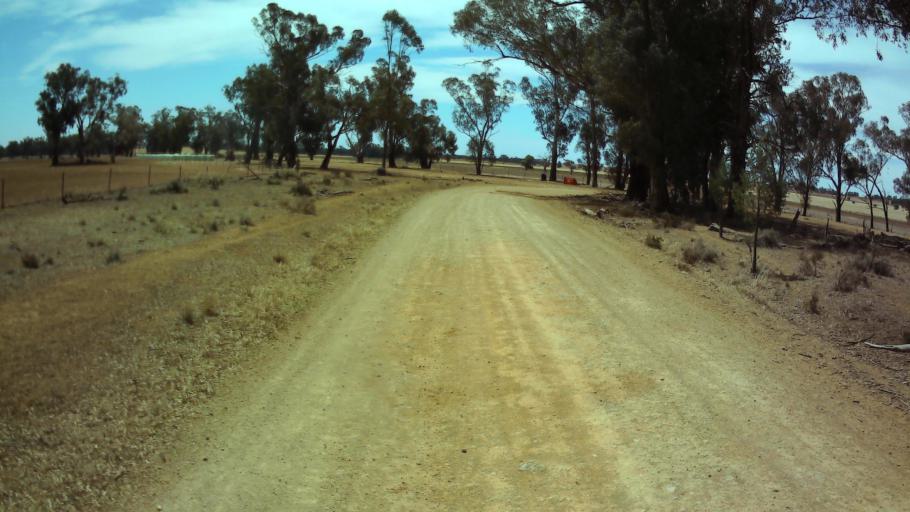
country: AU
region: New South Wales
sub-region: Weddin
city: Grenfell
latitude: -33.7591
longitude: 148.1403
